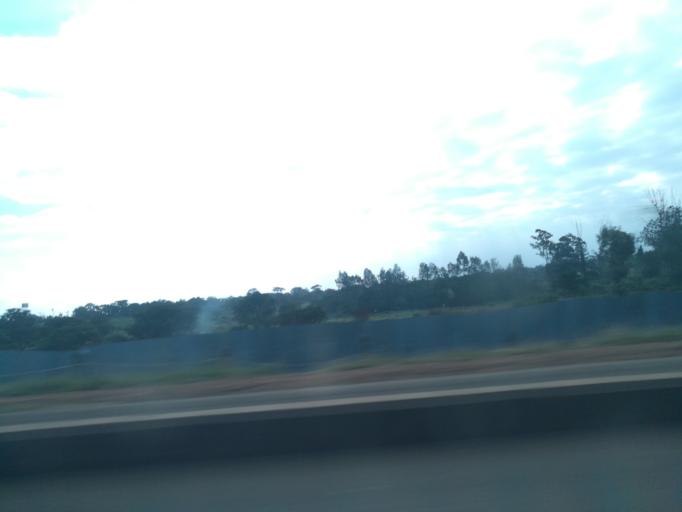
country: KE
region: Nairobi Area
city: Thika
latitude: -1.1149
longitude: 37.0111
